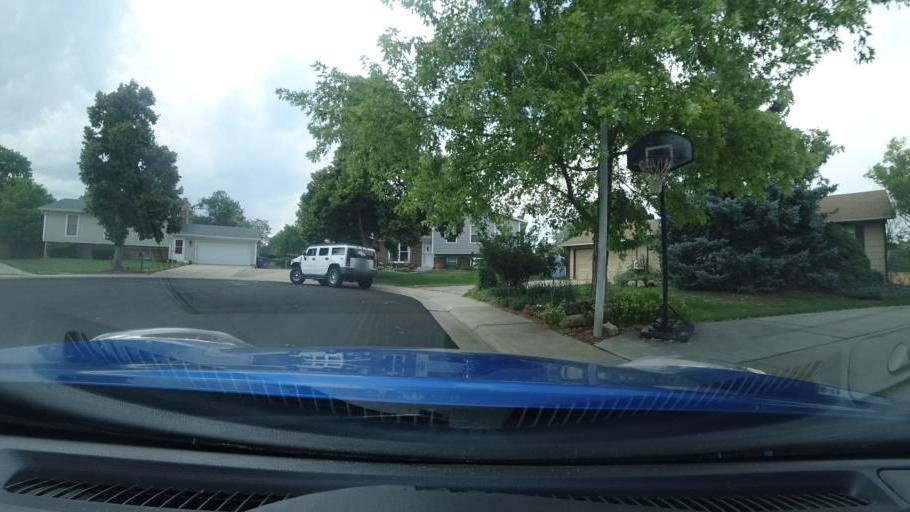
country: US
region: Colorado
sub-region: Adams County
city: Aurora
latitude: 39.6862
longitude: -104.7835
